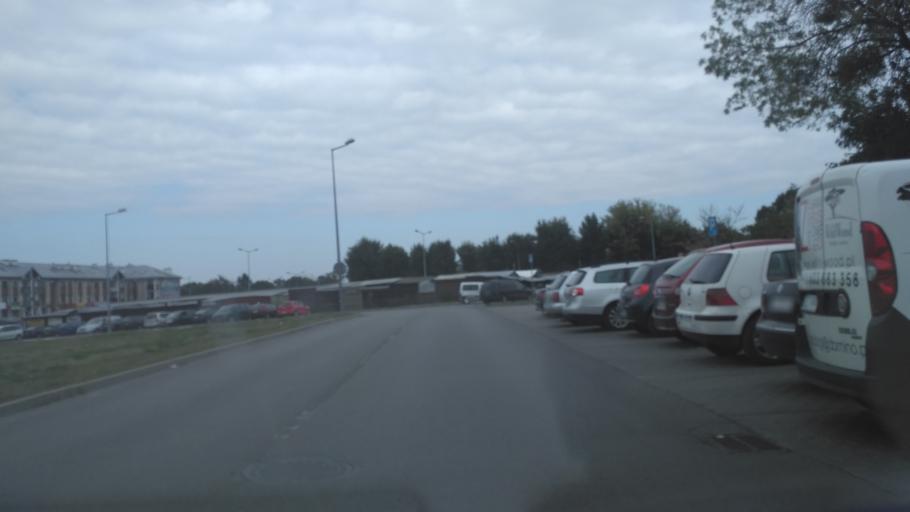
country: PL
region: Lublin Voivodeship
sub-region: Chelm
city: Chelm
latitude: 51.1286
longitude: 23.4663
